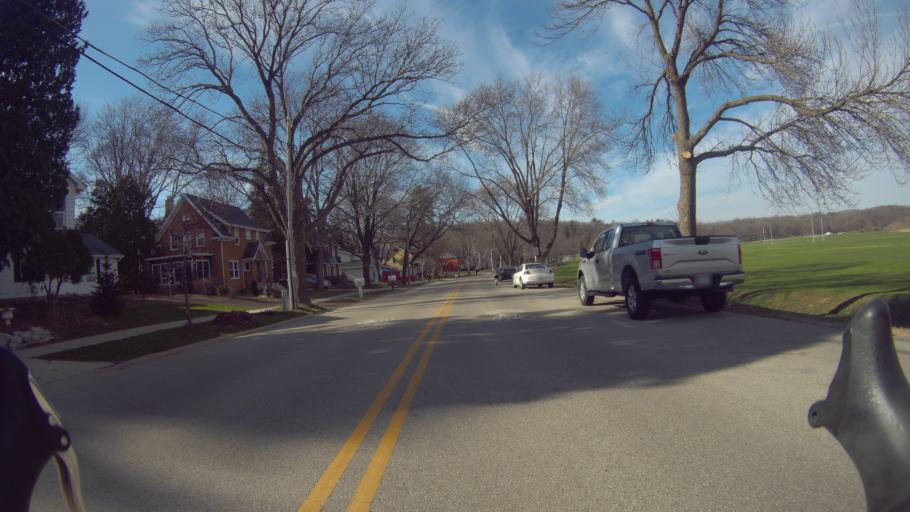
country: US
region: Wisconsin
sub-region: Dane County
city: Shorewood Hills
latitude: 43.0795
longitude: -89.4369
